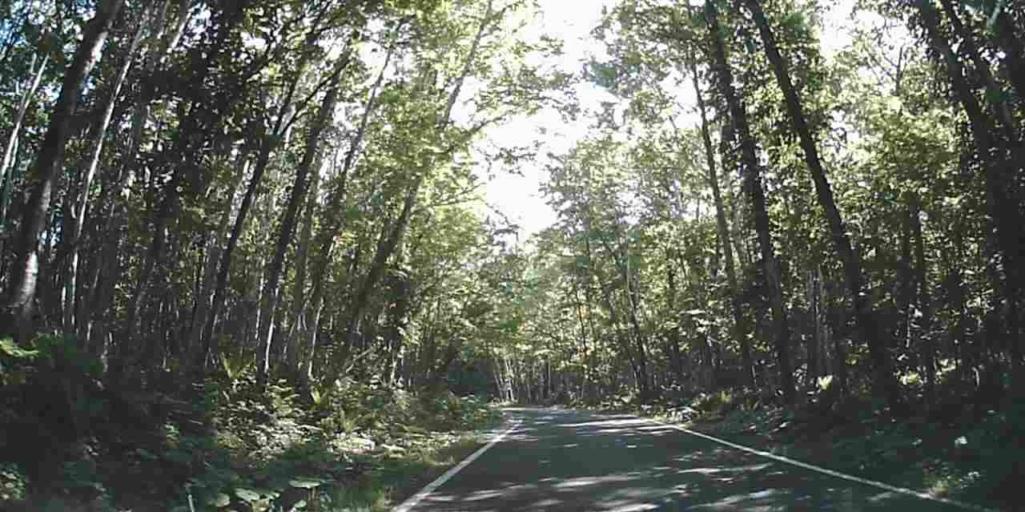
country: JP
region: Hokkaido
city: Shiraoi
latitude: 42.7199
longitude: 141.4112
